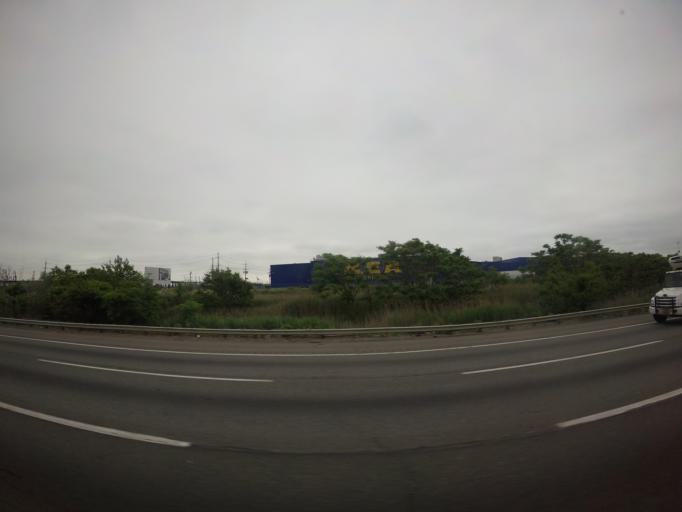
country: US
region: New Jersey
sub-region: Union County
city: Elizabeth
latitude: 40.6771
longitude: -74.1710
